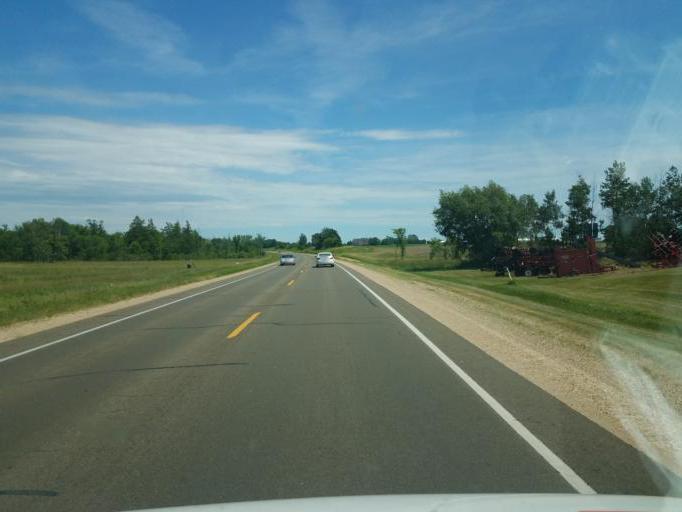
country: US
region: Wisconsin
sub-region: Sauk County
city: Reedsburg
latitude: 43.5454
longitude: -90.0505
